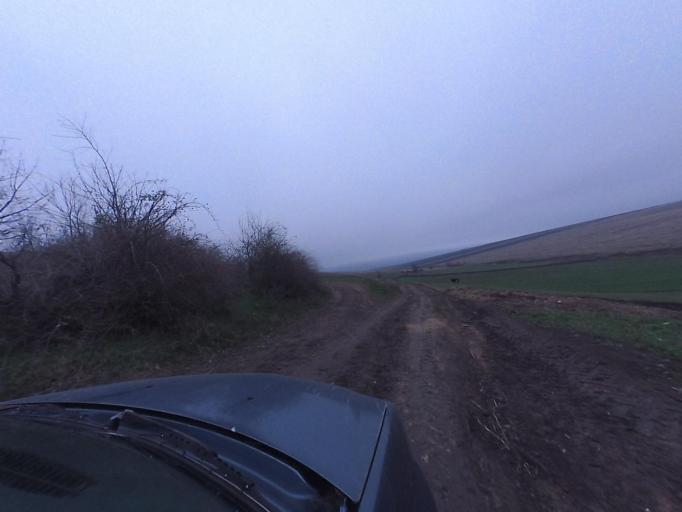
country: RO
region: Galati
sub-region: Comuna Balabanesti
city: Balabanesti
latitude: 46.1347
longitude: 27.7501
